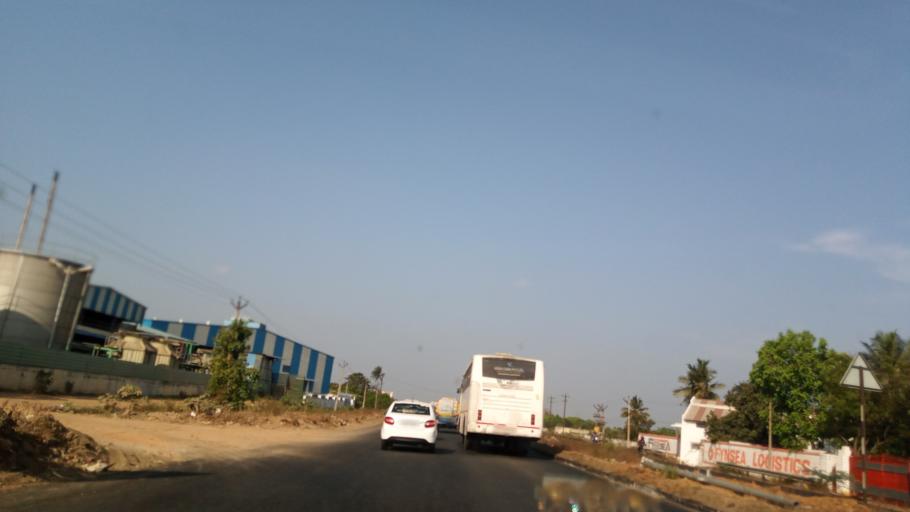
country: IN
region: Tamil Nadu
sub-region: Kancheepuram
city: Nandambakkam
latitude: 13.0165
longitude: 80.0067
